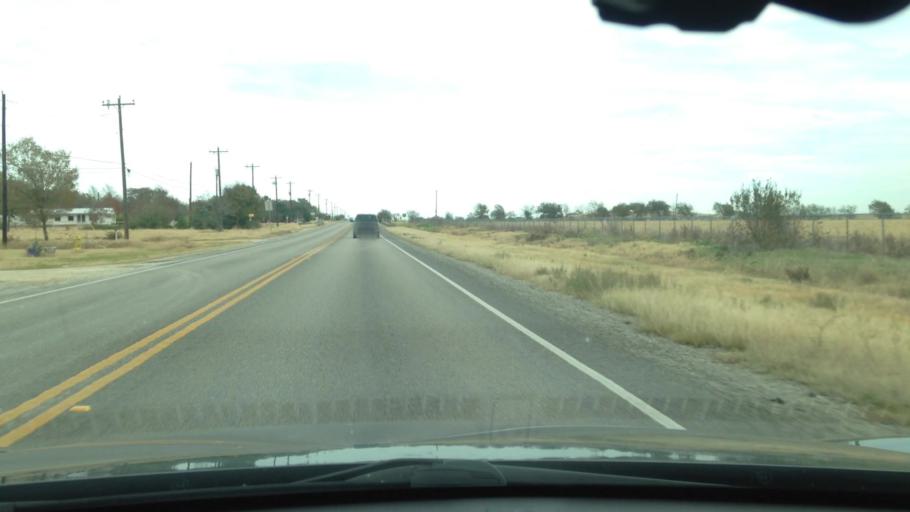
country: US
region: Texas
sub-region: Caldwell County
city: Martindale
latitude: 29.9083
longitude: -97.8603
